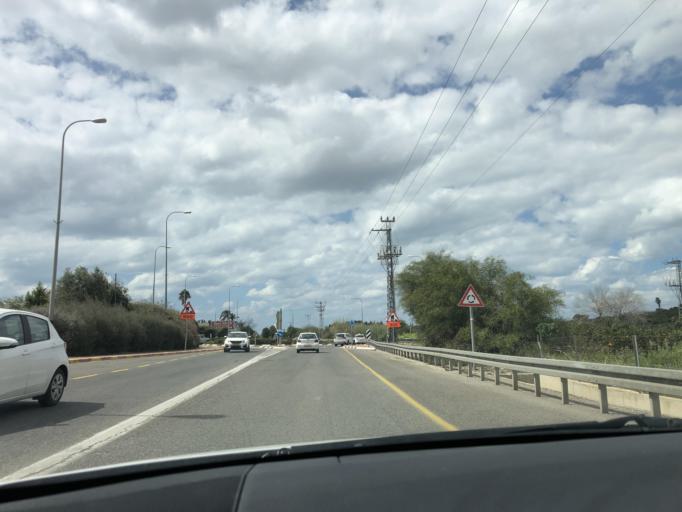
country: IL
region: Central District
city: Tel Mond
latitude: 32.2613
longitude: 34.9262
